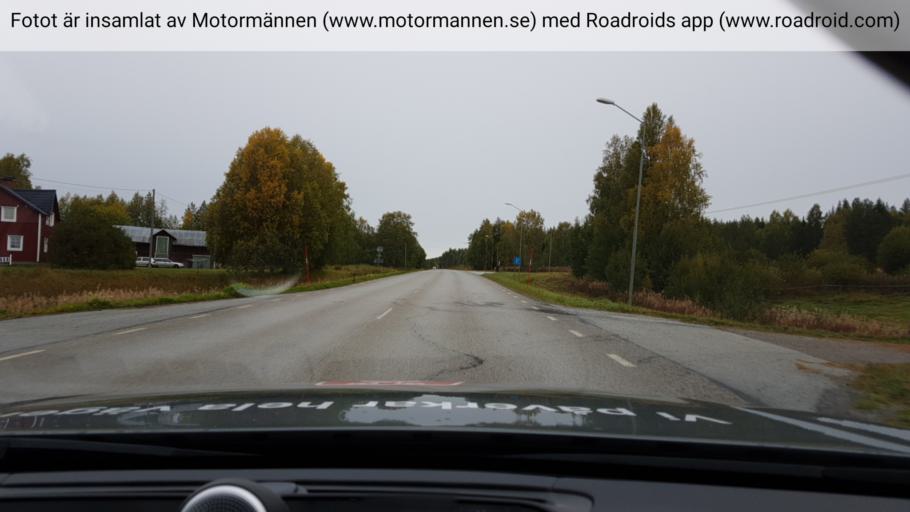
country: SE
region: Jaemtland
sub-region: Stroemsunds Kommun
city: Stroemsund
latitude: 63.8912
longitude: 15.5405
